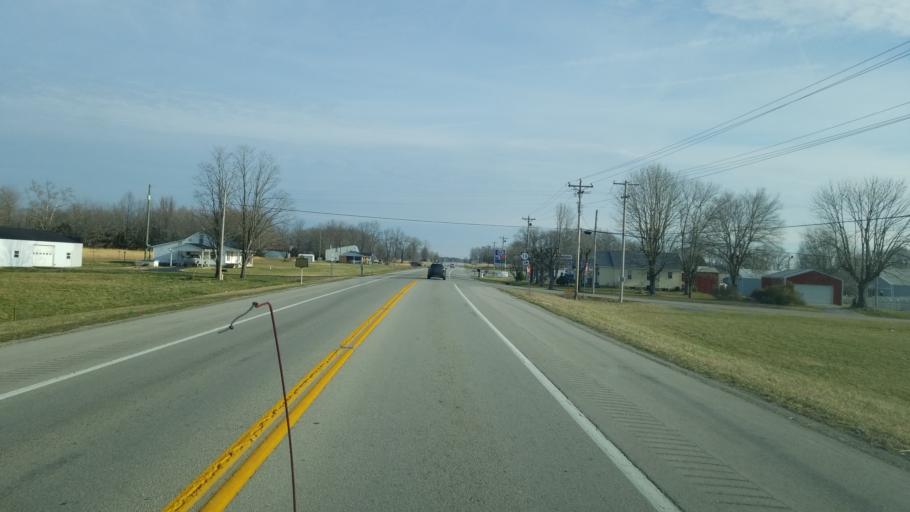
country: US
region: Kentucky
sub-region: Russell County
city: Russell Springs
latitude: 37.1218
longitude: -85.0455
